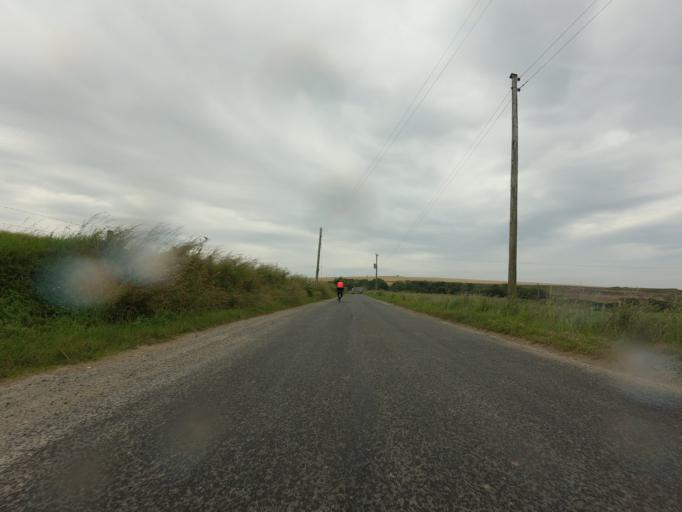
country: GB
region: Scotland
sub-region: Aberdeenshire
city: Portsoy
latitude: 57.6761
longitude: -2.6491
